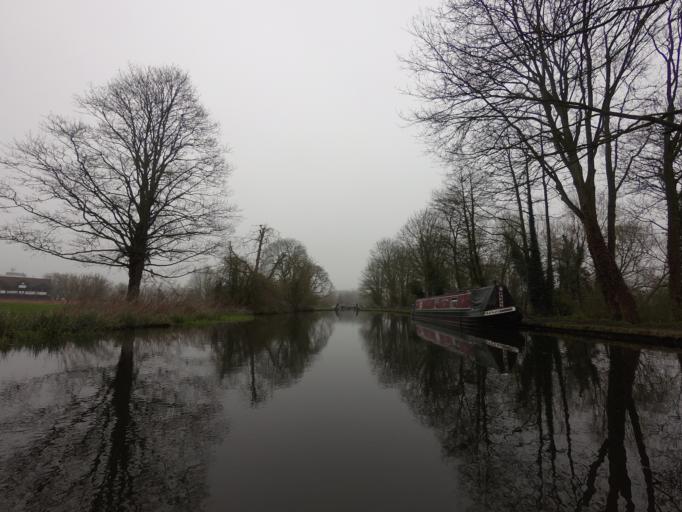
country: GB
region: England
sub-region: Hertfordshire
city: Hemel Hempstead
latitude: 51.7433
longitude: -0.4774
